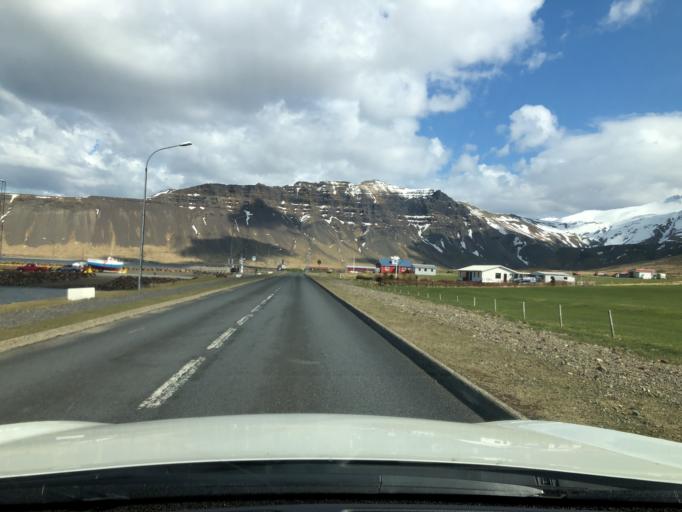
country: IS
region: West
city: Olafsvik
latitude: 64.9215
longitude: -23.2506
